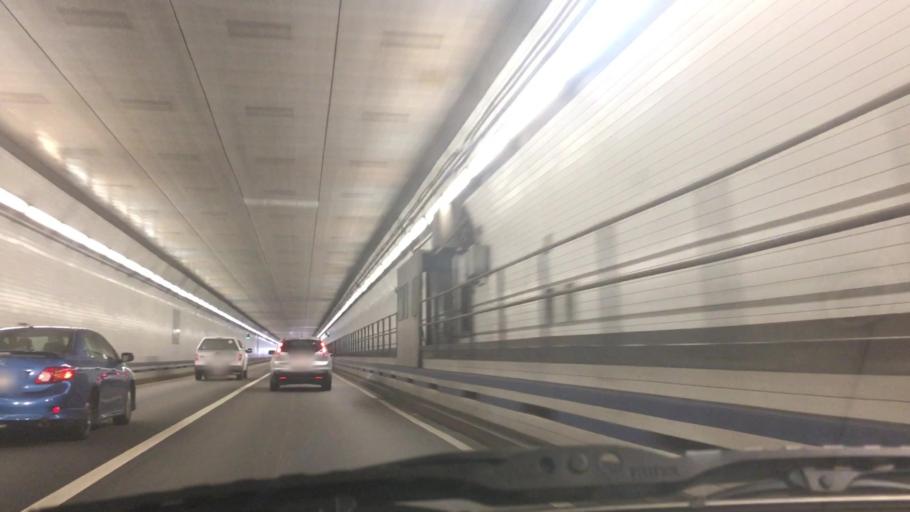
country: US
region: Virginia
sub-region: City of Hampton
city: East Hampton
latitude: 36.9870
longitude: -76.3060
